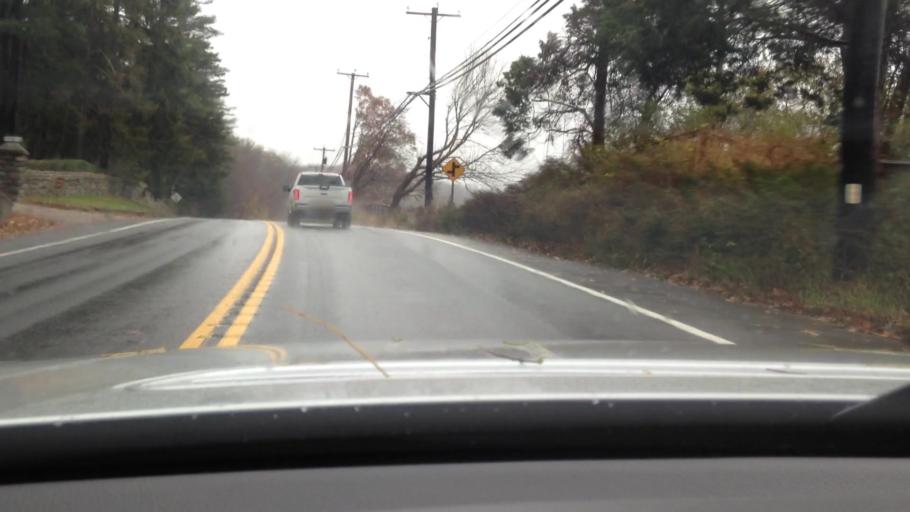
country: US
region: New York
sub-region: Orange County
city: Highland Falls
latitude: 41.3452
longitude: -73.9265
